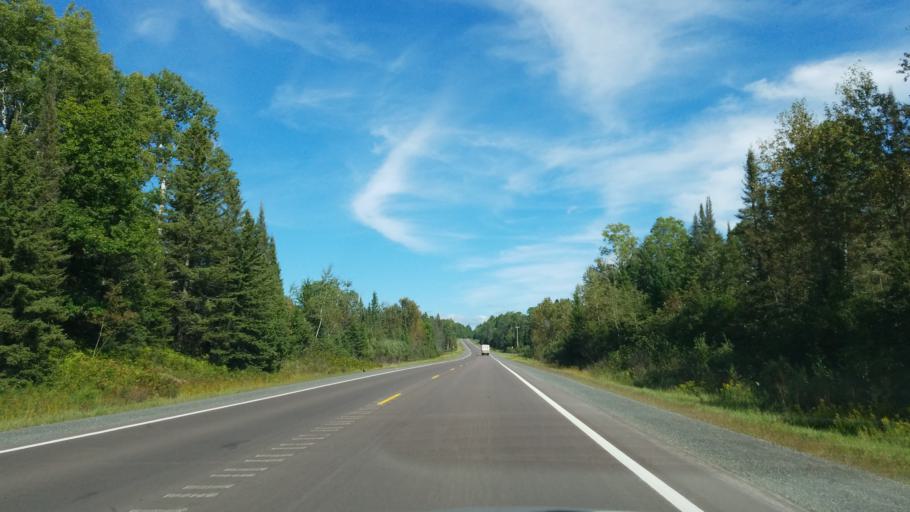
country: US
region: Michigan
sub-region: Baraga County
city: Baraga
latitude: 46.4957
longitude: -88.8132
